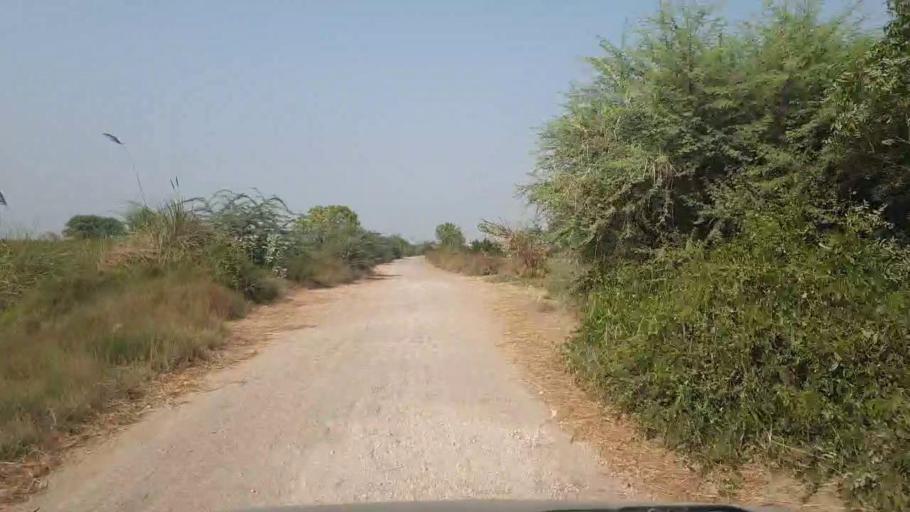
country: PK
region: Sindh
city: Tando Muhammad Khan
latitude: 25.0924
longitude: 68.3386
